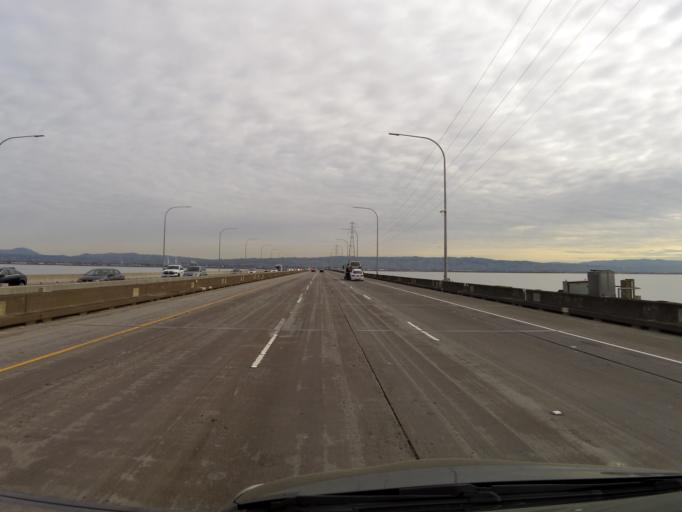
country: US
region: California
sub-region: Alameda County
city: San Lorenzo
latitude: 37.6109
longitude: -122.1749
